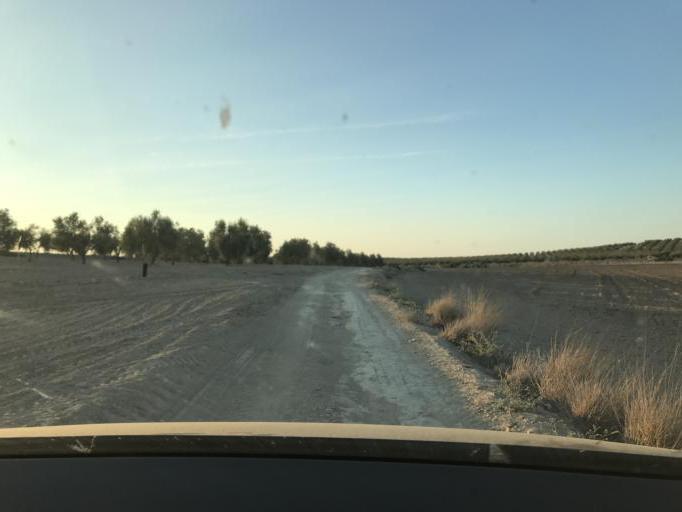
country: ES
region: Andalusia
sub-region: Provincia de Sevilla
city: Osuna
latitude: 37.2326
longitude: -5.0587
